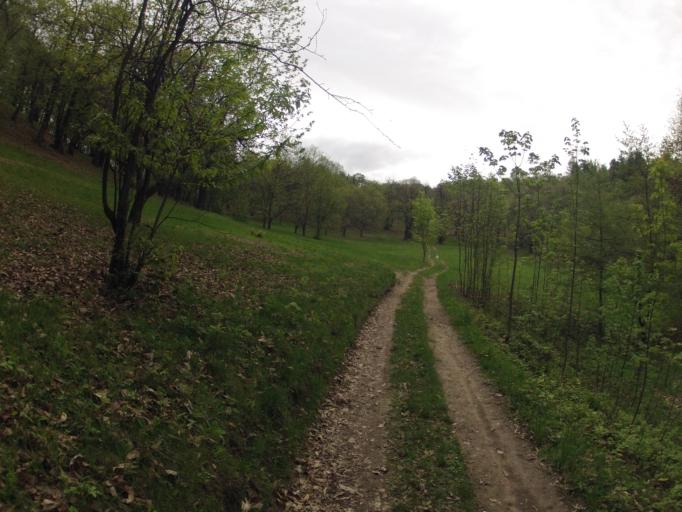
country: IT
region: Piedmont
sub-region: Provincia di Cuneo
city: Peveragno
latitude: 44.3188
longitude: 7.5849
